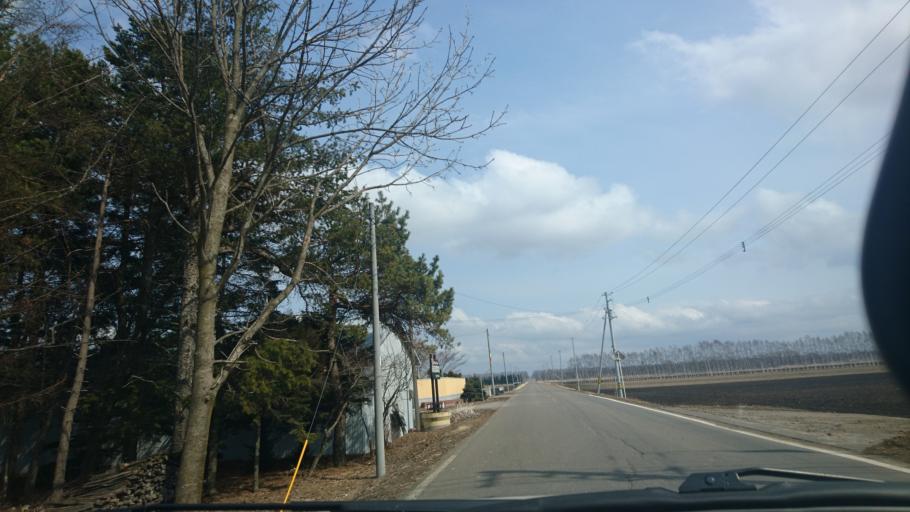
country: JP
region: Hokkaido
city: Otofuke
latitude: 43.2069
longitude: 143.2754
